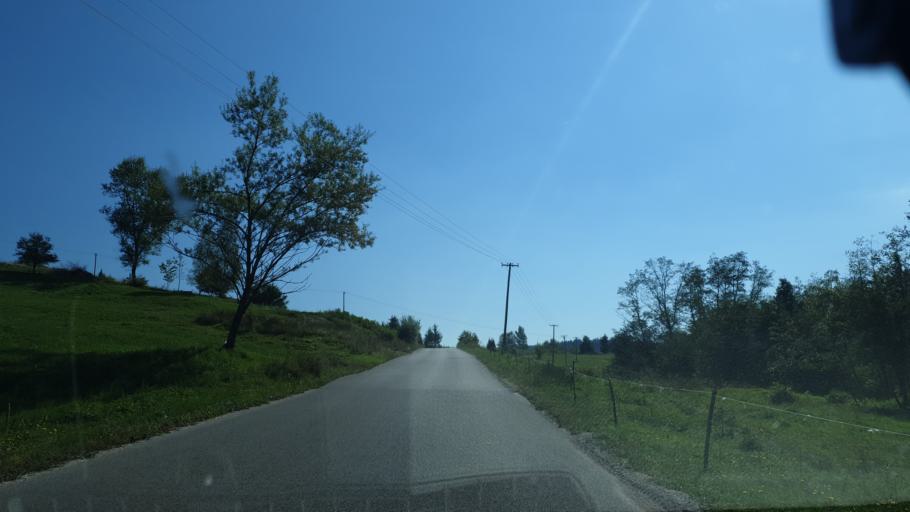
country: RS
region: Central Serbia
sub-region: Zlatiborski Okrug
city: Nova Varos
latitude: 43.4376
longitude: 19.8677
